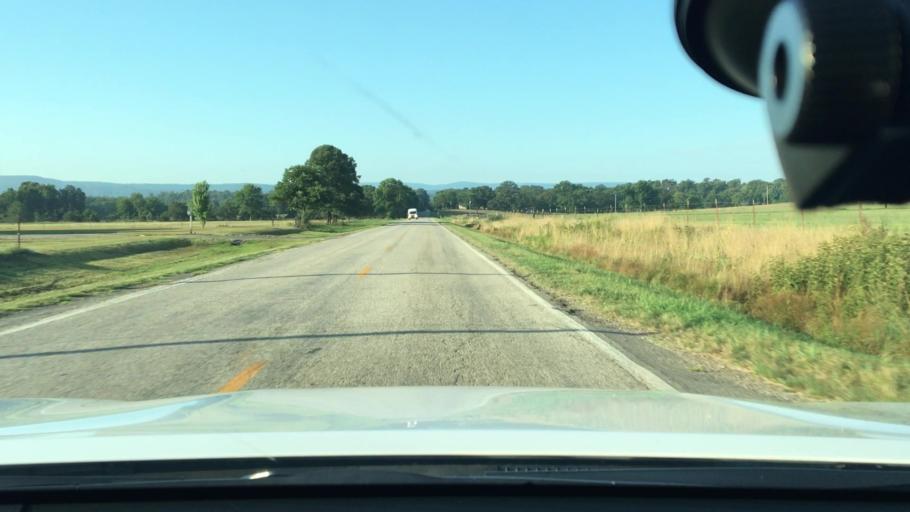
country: US
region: Arkansas
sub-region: Logan County
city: Paris
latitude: 35.3230
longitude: -93.6322
